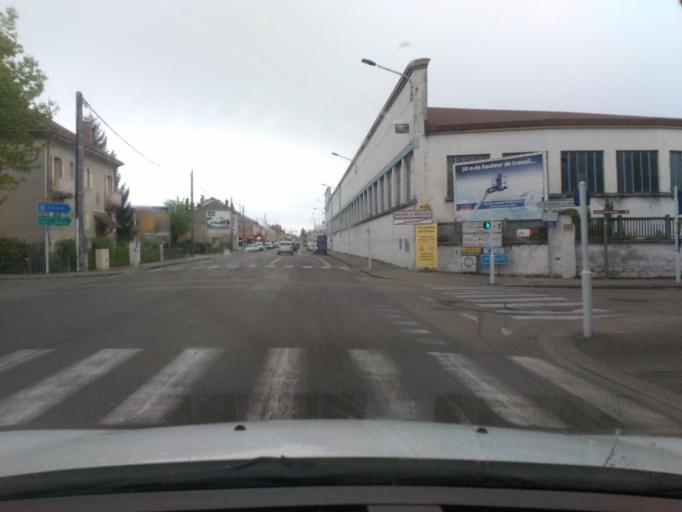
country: FR
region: Rhone-Alpes
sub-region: Departement de l'Ain
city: Peronnas
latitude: 46.1917
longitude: 5.2123
